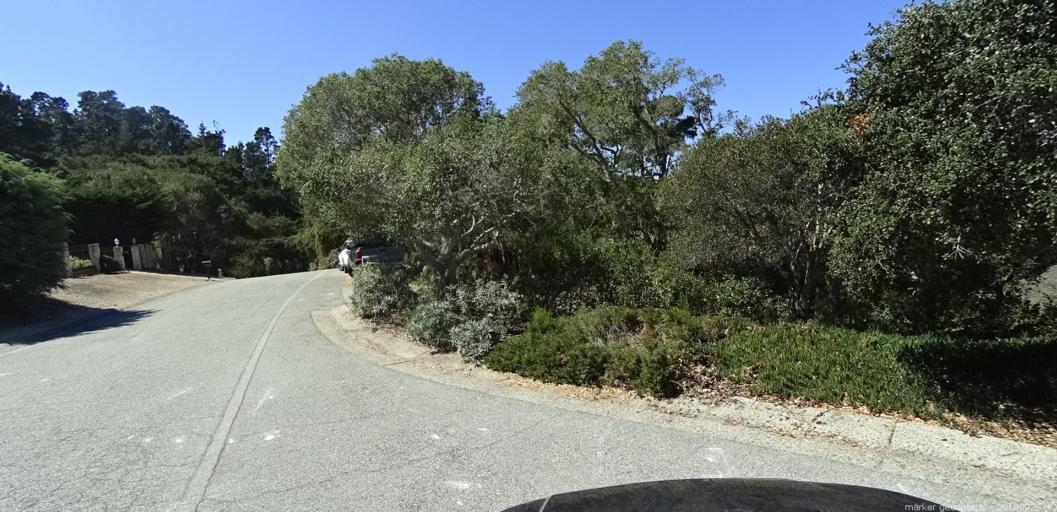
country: US
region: California
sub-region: Monterey County
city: Monterey
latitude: 36.5766
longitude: -121.8874
